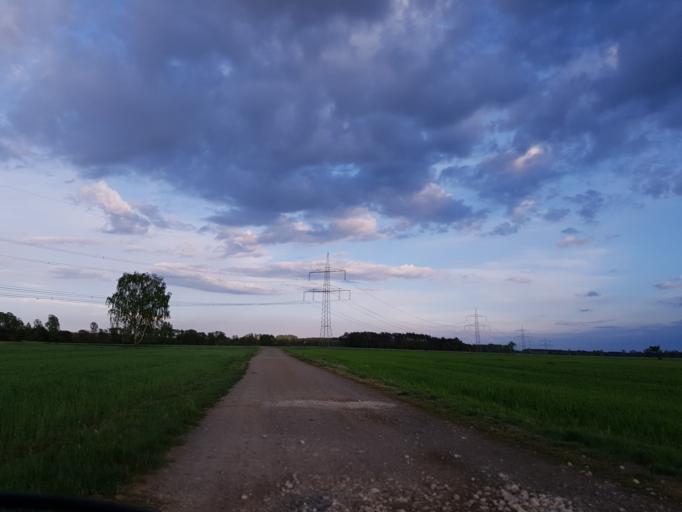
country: DE
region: Brandenburg
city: Schilda
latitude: 51.5679
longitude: 13.3873
